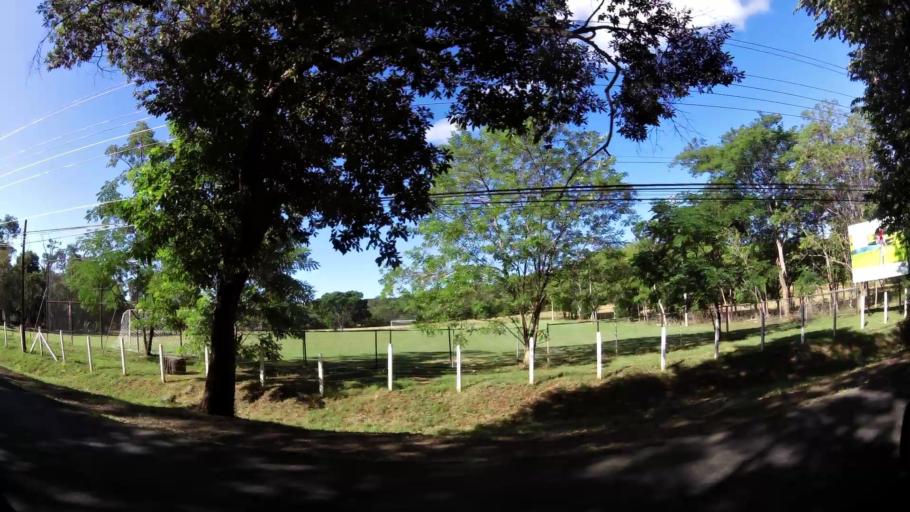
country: CR
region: Guanacaste
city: Sardinal
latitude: 10.3869
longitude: -85.7905
